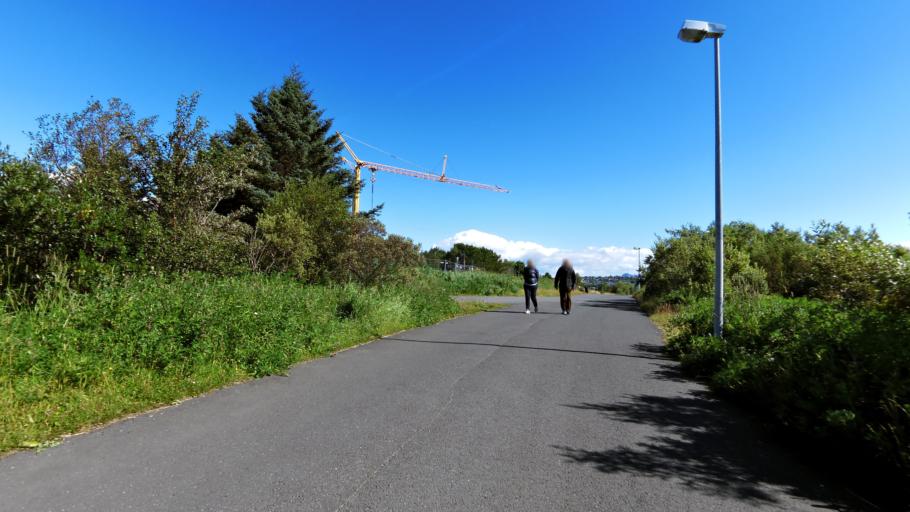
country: IS
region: Capital Region
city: Kopavogur
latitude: 64.1224
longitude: -21.9232
